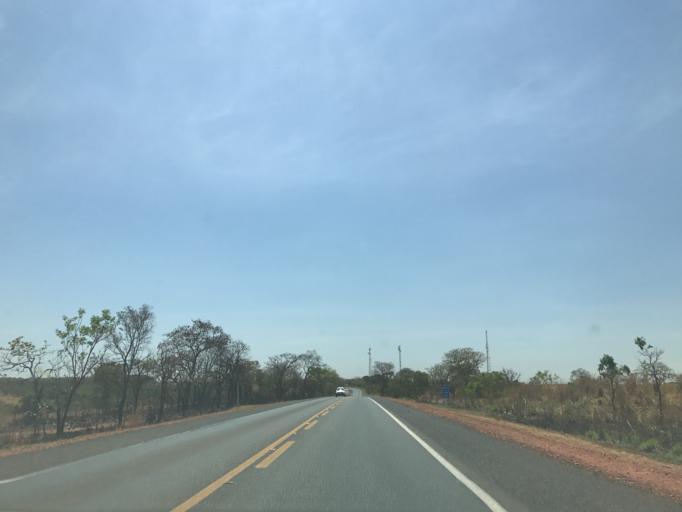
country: BR
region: Minas Gerais
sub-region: Frutal
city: Frutal
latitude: -19.8623
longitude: -48.9661
